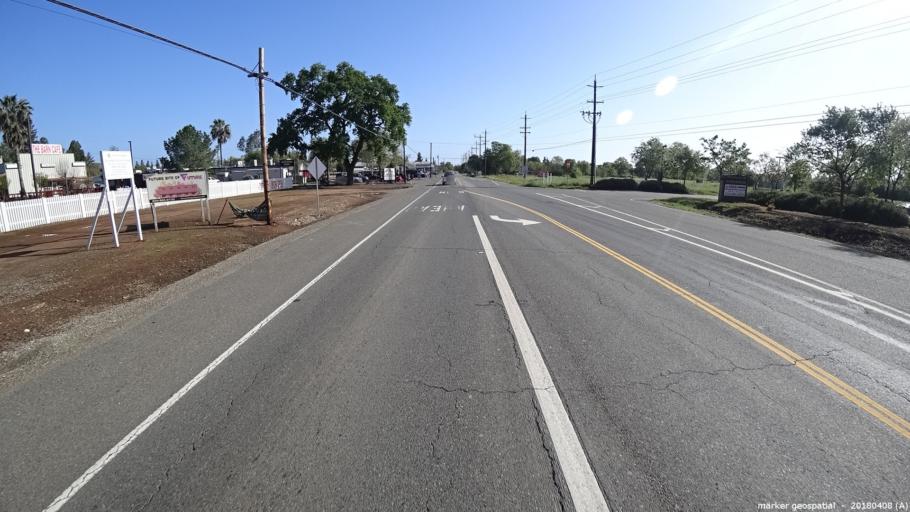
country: US
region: California
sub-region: Sacramento County
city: Wilton
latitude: 38.4318
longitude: -121.2997
